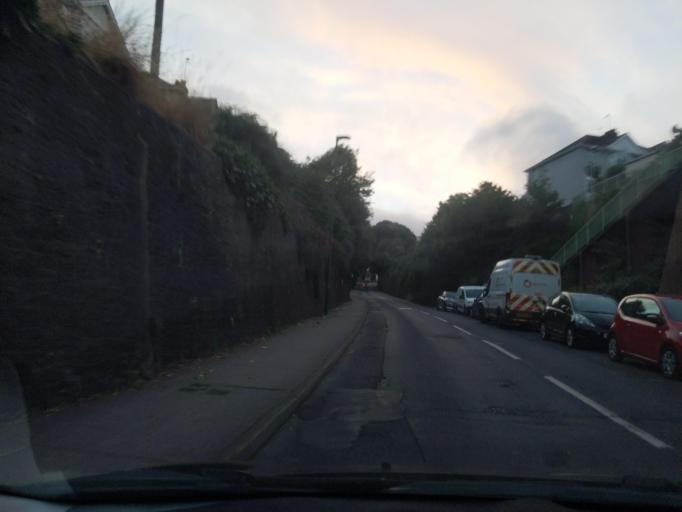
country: GB
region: England
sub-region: Borough of Torbay
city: Paignton
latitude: 50.4384
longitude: -3.5751
